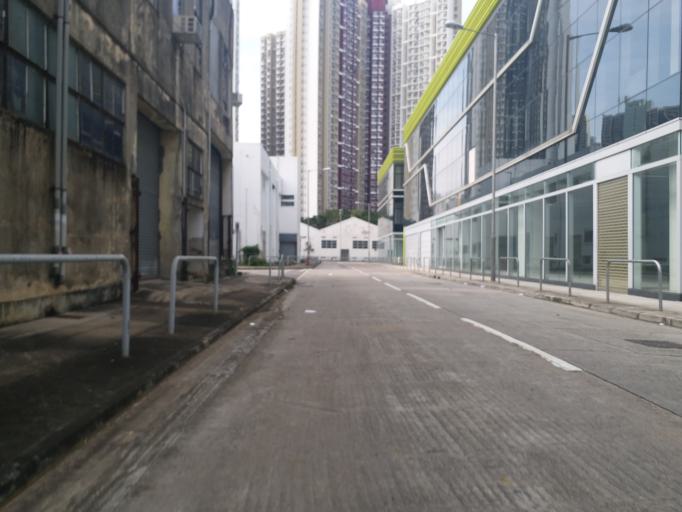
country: HK
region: Yuen Long
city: Yuen Long Kau Hui
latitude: 22.4432
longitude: 114.0033
